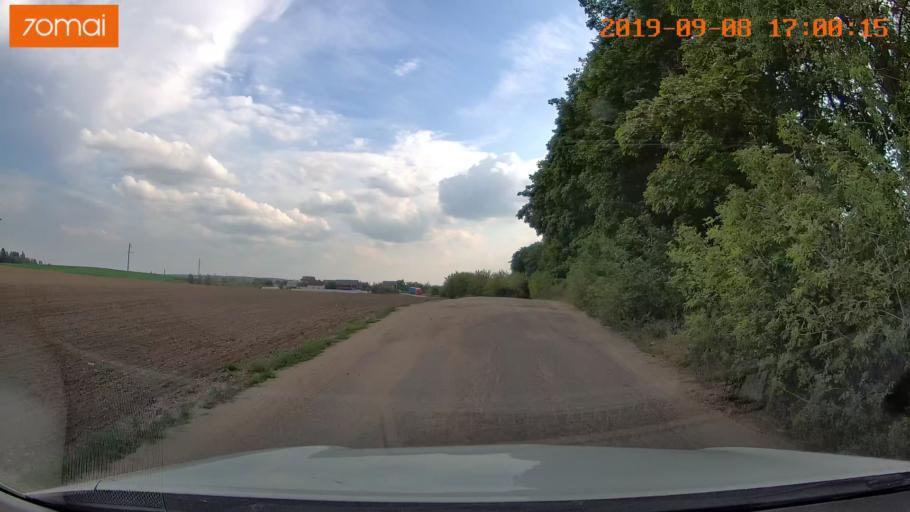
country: BY
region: Grodnenskaya
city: Hrodna
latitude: 53.7168
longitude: 23.9323
